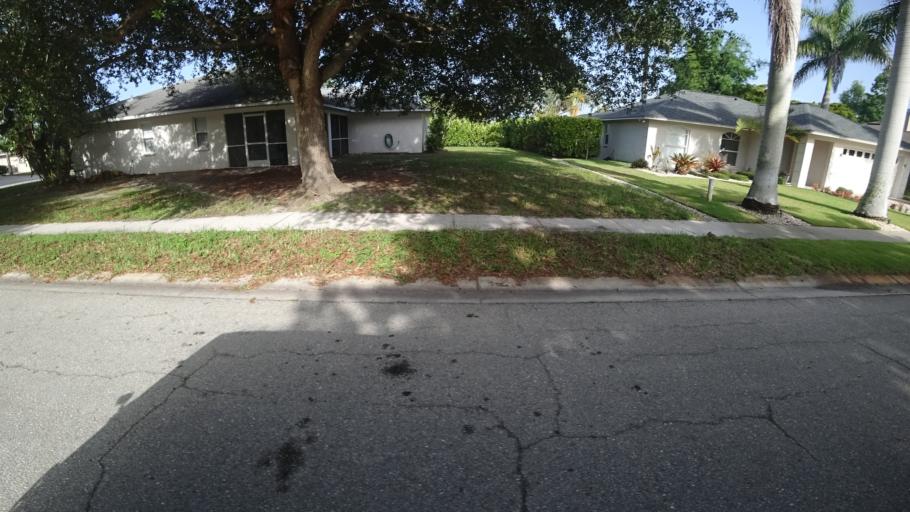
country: US
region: Florida
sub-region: Sarasota County
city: Desoto Lakes
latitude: 27.4237
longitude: -82.4715
